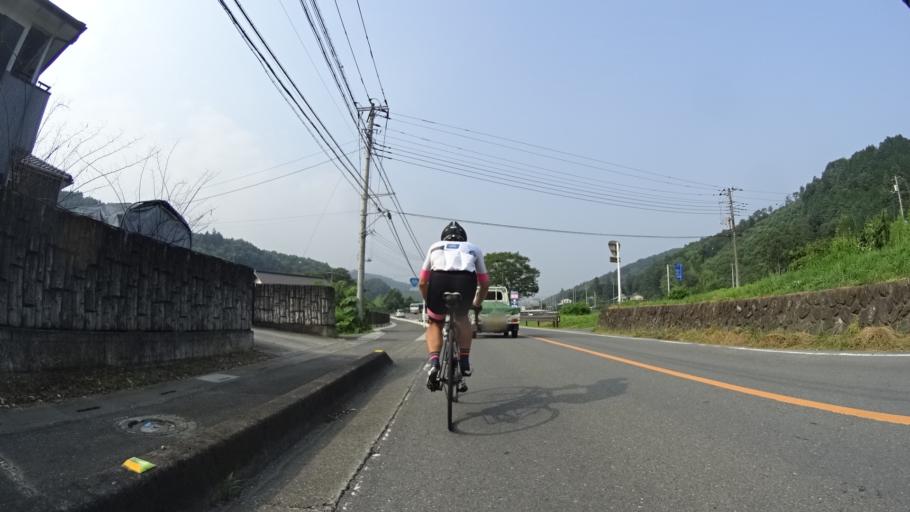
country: JP
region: Saitama
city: Chichibu
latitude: 36.0275
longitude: 139.0717
